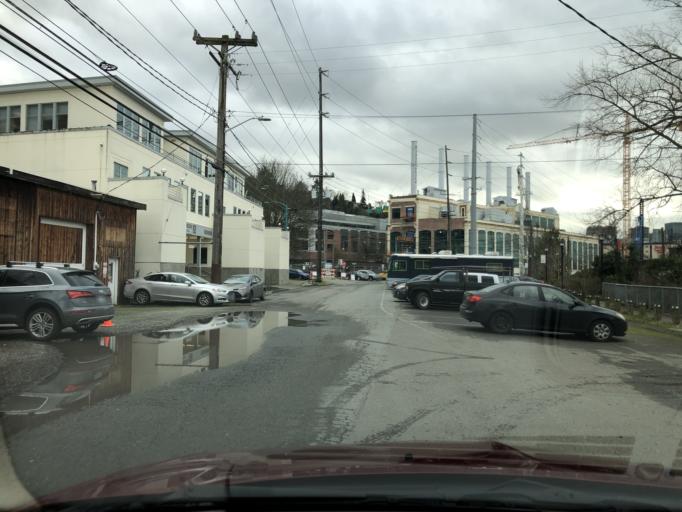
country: US
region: Washington
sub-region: King County
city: Seattle
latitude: 47.6330
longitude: -122.3268
